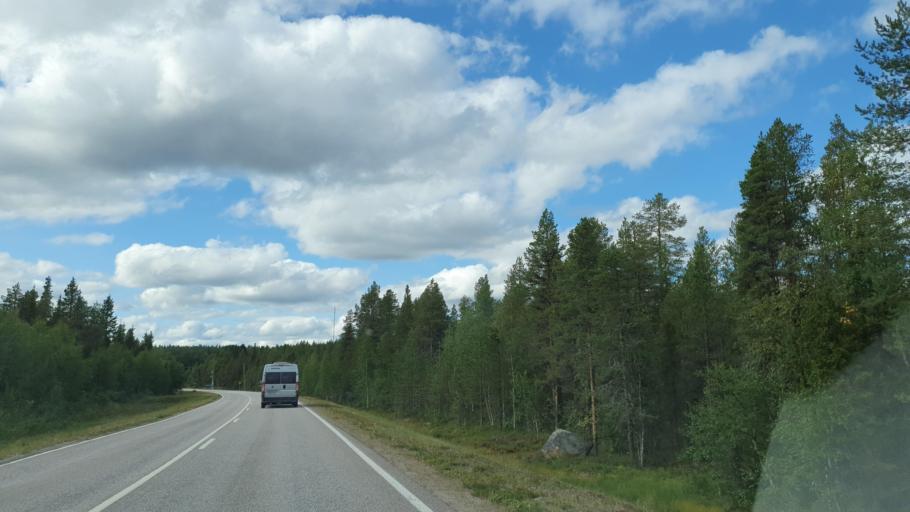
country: FI
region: Lapland
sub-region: Tunturi-Lappi
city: Muonio
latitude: 67.8605
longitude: 24.1304
